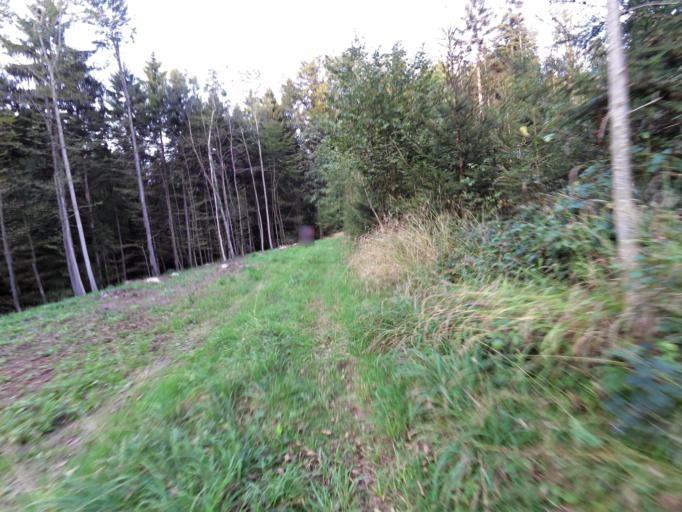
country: CH
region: Thurgau
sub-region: Frauenfeld District
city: Frauenfeld
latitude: 47.5307
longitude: 8.8877
